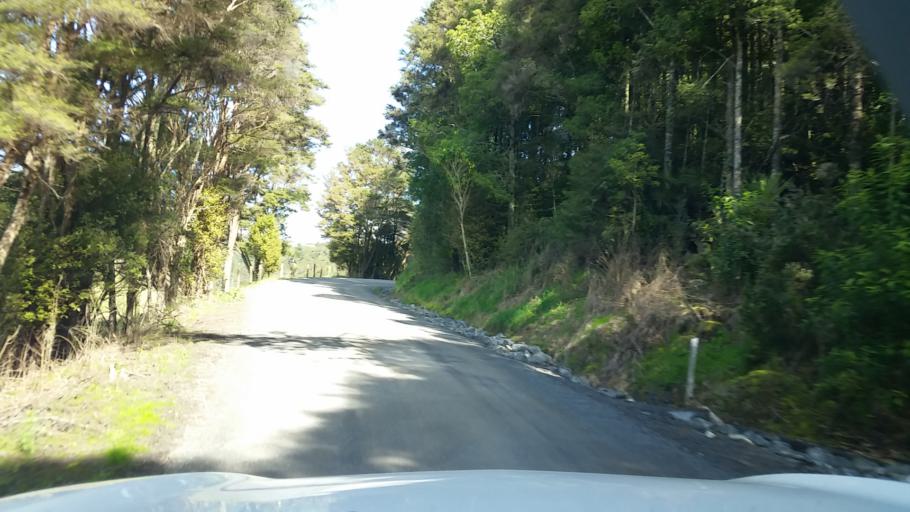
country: NZ
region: Waikato
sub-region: Hauraki District
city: Ngatea
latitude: -37.4475
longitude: 175.4841
